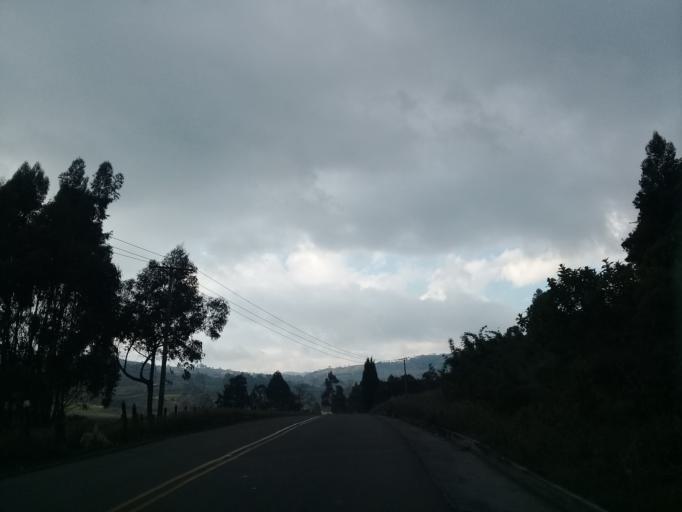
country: CO
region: Cundinamarca
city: Zipaquira
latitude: 5.0655
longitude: -74.0545
